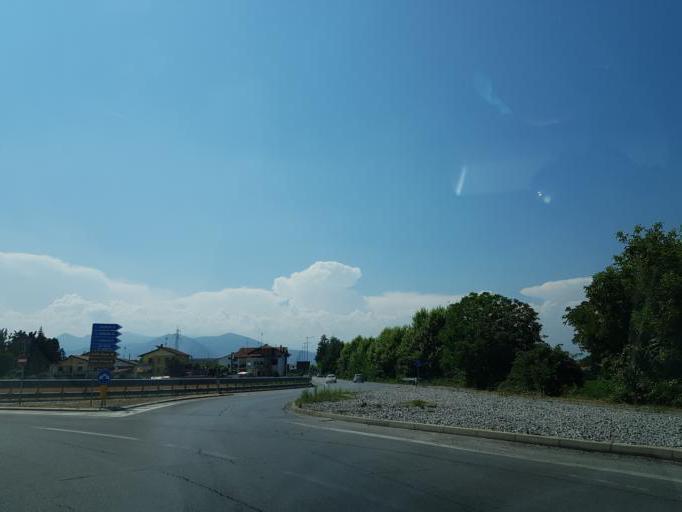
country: IT
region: Piedmont
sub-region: Provincia di Cuneo
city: San Defendente
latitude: 44.3948
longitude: 7.5118
